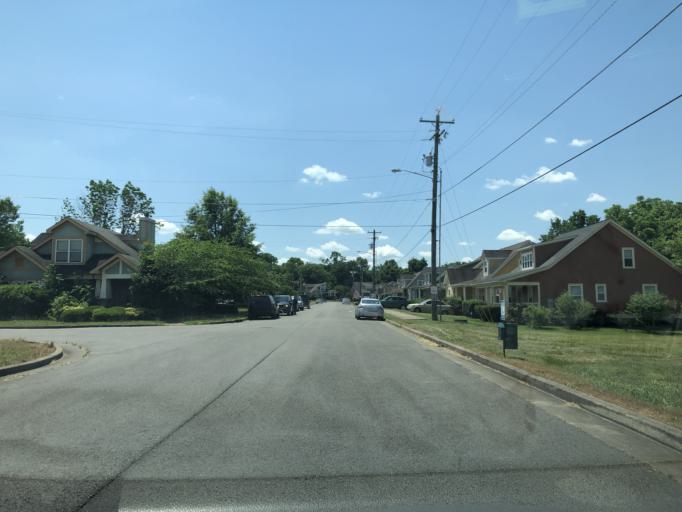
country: US
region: Tennessee
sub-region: Davidson County
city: Goodlettsville
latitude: 36.2617
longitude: -86.6980
